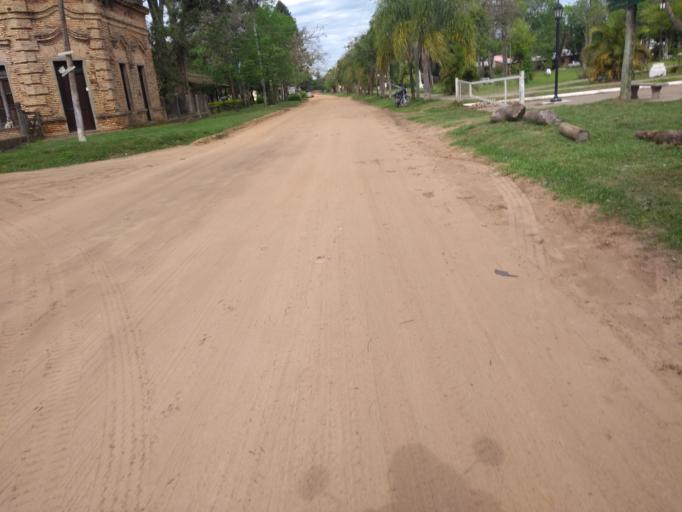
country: AR
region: Corrientes
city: San Luis del Palmar
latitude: -27.4563
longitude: -58.6596
